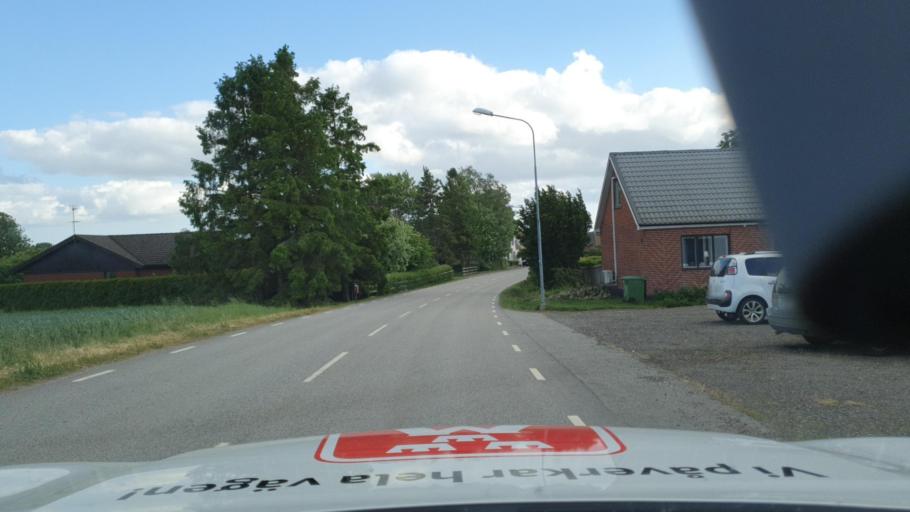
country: SE
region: Skane
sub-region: Tomelilla Kommun
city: Tomelilla
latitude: 55.5845
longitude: 14.0168
